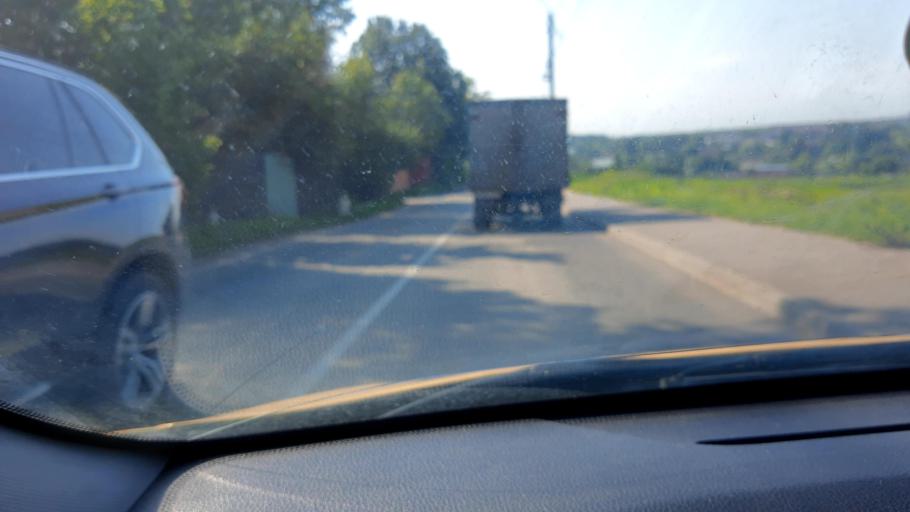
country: RU
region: Moscow
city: Zagor'ye
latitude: 55.5576
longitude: 37.6653
